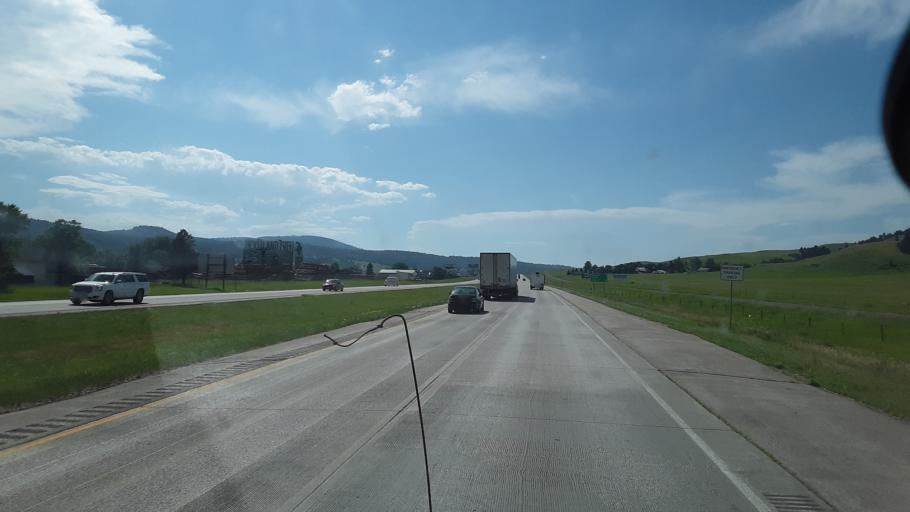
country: US
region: South Dakota
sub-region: Meade County
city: Sturgis
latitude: 44.4225
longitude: -103.5440
